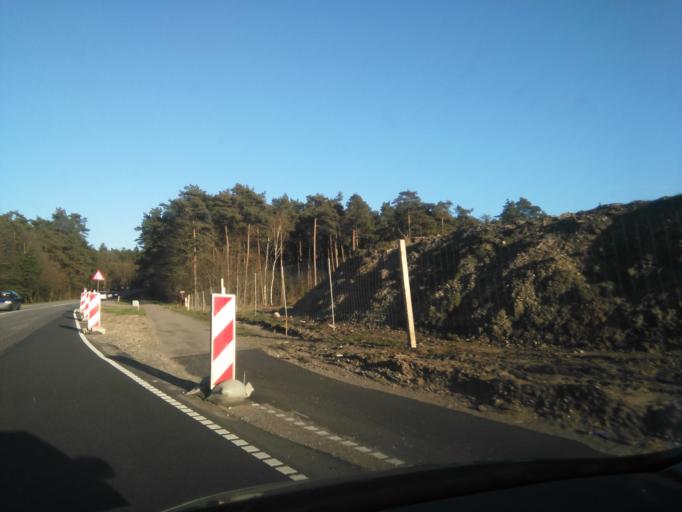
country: DK
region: Central Jutland
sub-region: Silkeborg Kommune
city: Svejbaek
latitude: 56.1618
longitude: 9.6150
